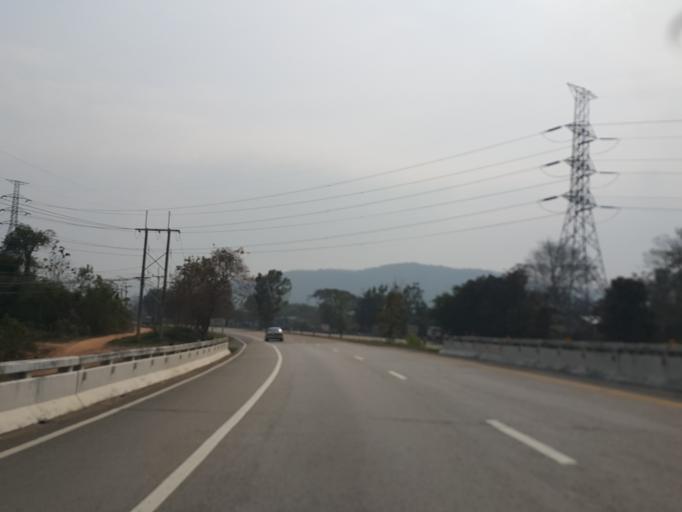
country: TH
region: Lamphun
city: Mae Tha
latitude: 18.4631
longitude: 99.1584
